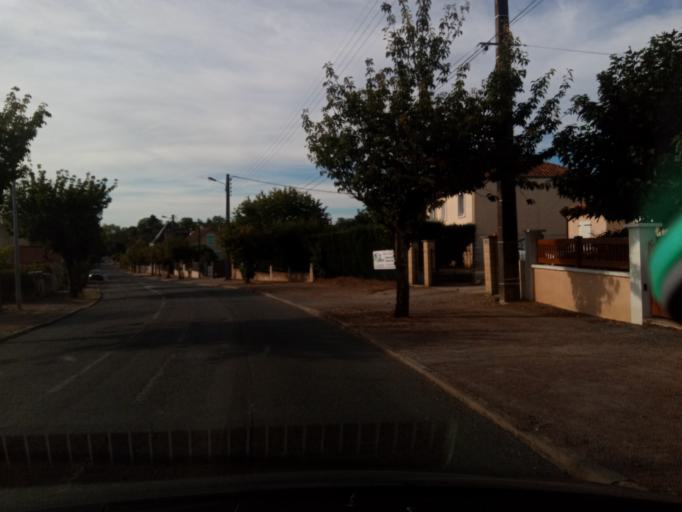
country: FR
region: Poitou-Charentes
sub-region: Departement de la Vienne
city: Montmorillon
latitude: 46.4184
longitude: 0.8794
